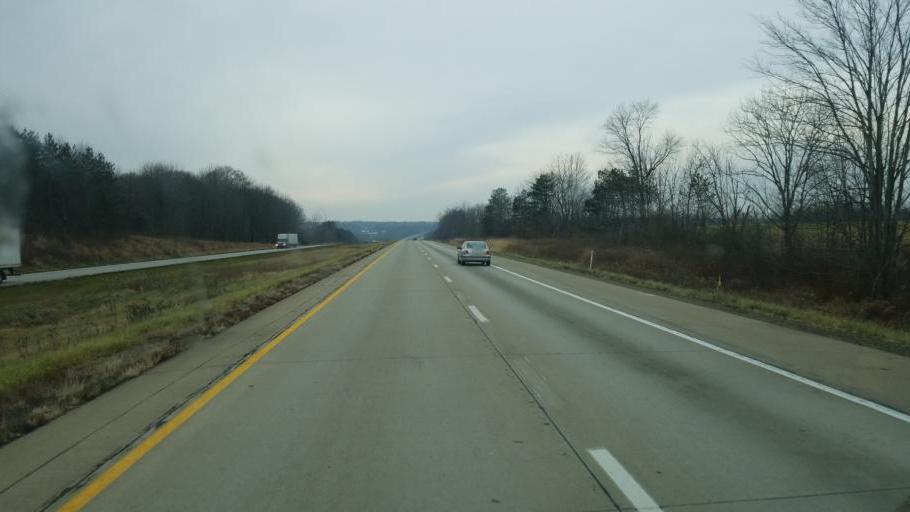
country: US
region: Pennsylvania
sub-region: Lawrence County
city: New Wilmington
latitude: 41.1849
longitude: -80.3732
